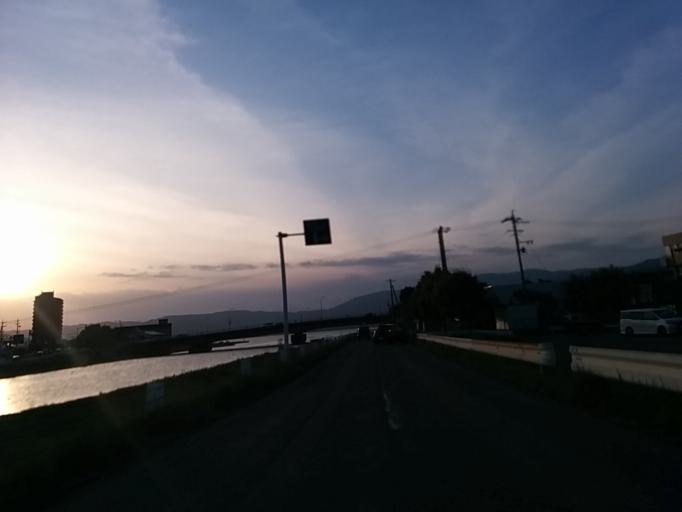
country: JP
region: Nagano
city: Suwa
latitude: 36.0374
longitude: 138.1027
